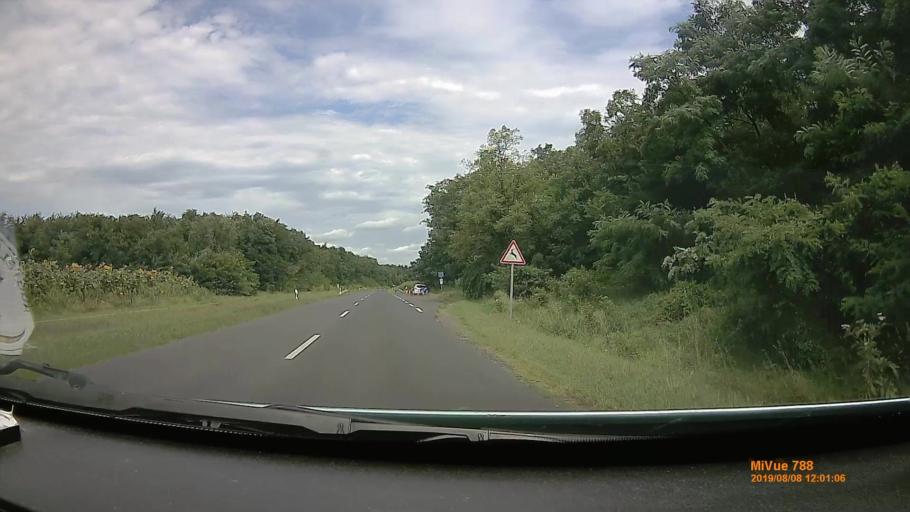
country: HU
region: Szabolcs-Szatmar-Bereg
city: Nyirbogat
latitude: 47.7867
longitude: 22.0361
